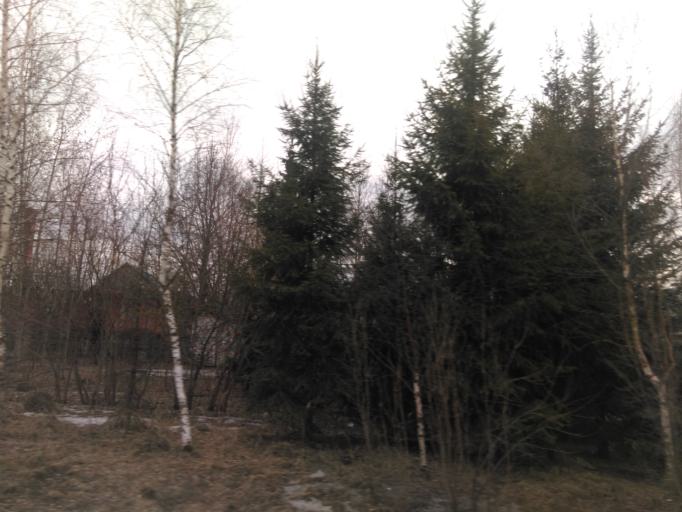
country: RU
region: Moskovskaya
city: Zvenigorod
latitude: 55.7350
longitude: 36.9360
